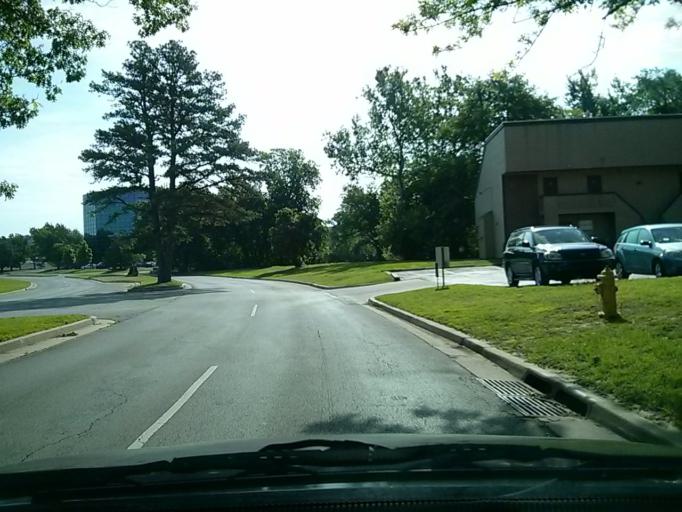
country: US
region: Oklahoma
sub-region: Tulsa County
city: Jenks
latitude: 36.0569
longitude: -95.9619
